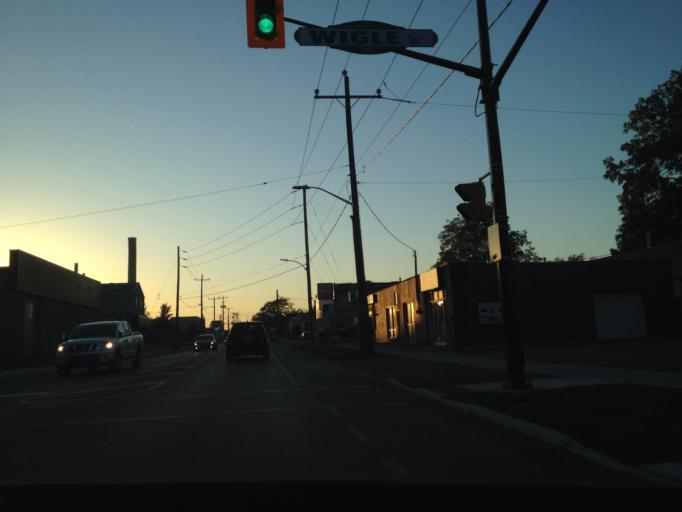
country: CA
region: Ontario
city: Amherstburg
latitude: 42.0464
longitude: -82.5945
